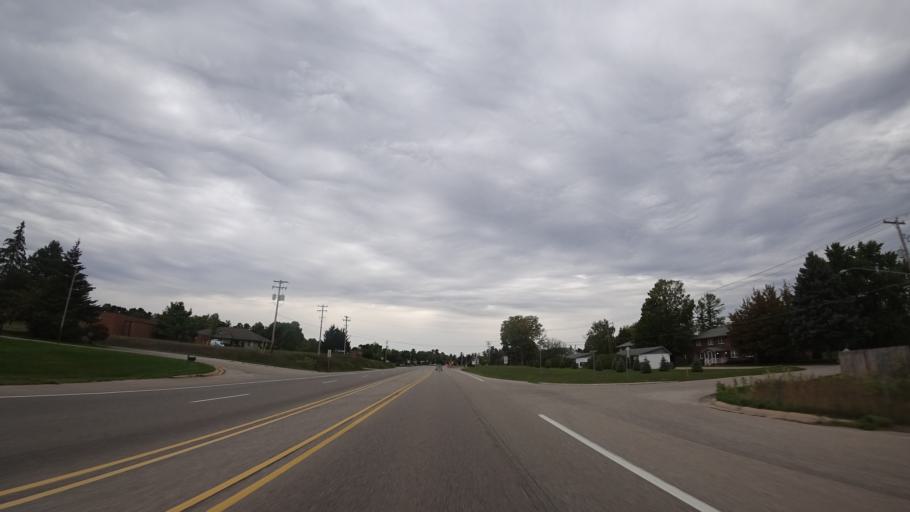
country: US
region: Michigan
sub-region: Grand Traverse County
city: Traverse City
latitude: 44.7732
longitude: -85.4943
